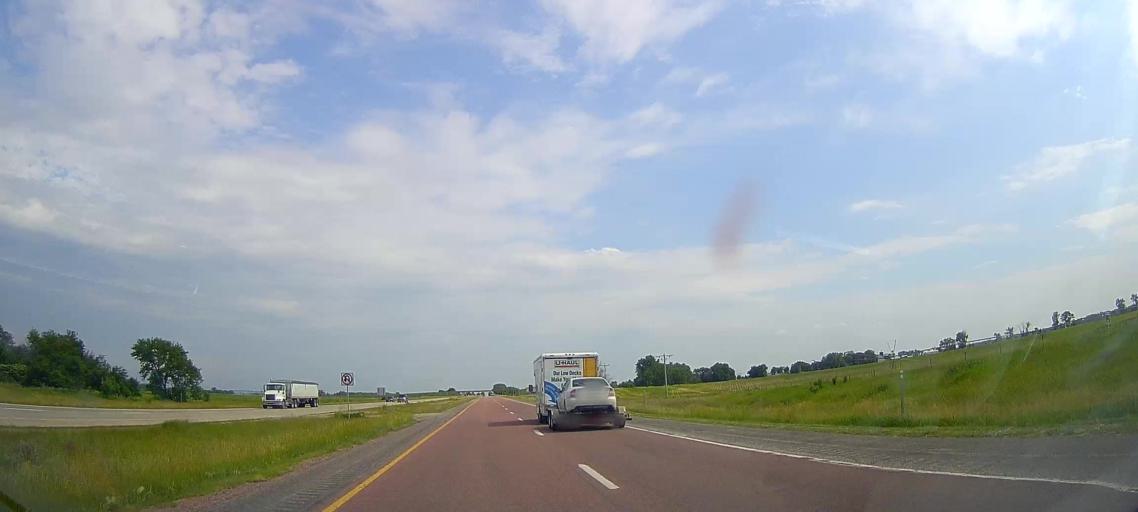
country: US
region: Iowa
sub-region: Monona County
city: Onawa
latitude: 41.9875
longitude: -96.1080
